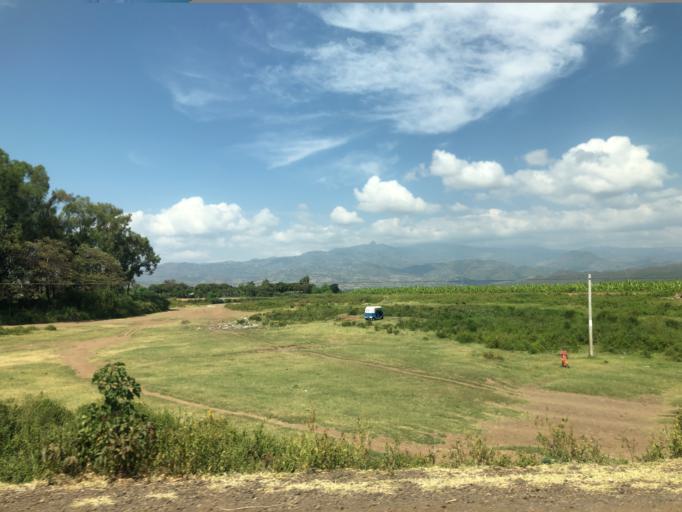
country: ET
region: Southern Nations, Nationalities, and People's Region
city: Arba Minch'
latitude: 5.8682
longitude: 37.4802
